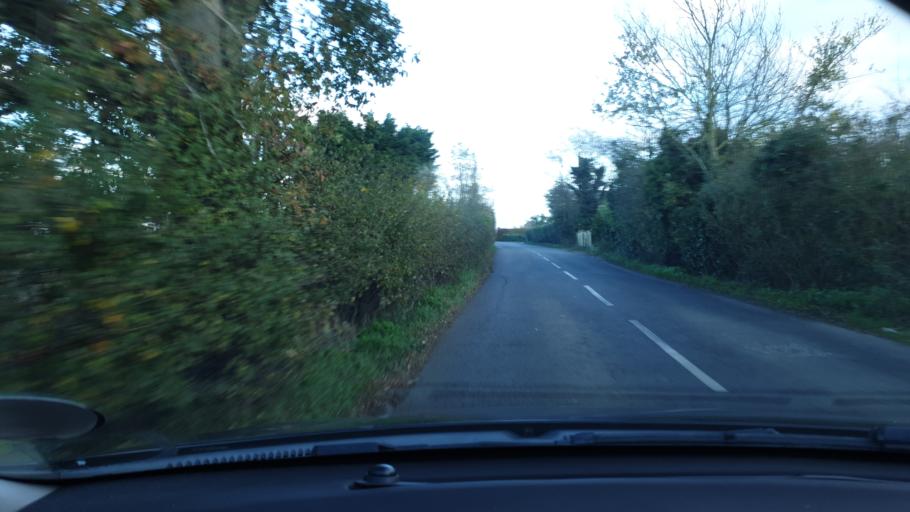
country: GB
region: England
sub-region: Essex
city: Little Clacton
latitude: 51.8987
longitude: 1.1415
